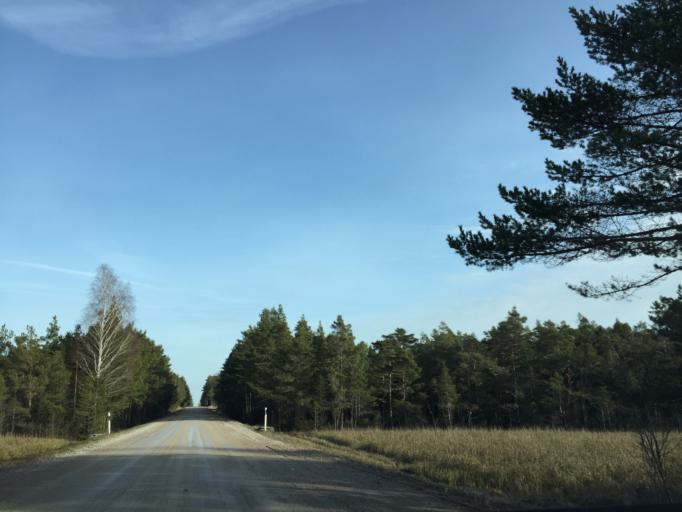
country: EE
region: Saare
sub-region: Kuressaare linn
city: Kuressaare
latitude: 58.3118
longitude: 21.9805
